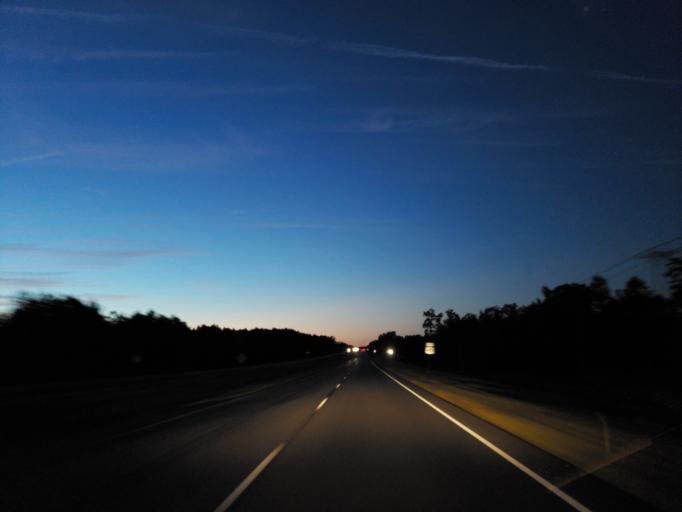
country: US
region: Mississippi
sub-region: Clarke County
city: Quitman
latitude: 32.0679
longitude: -88.6829
